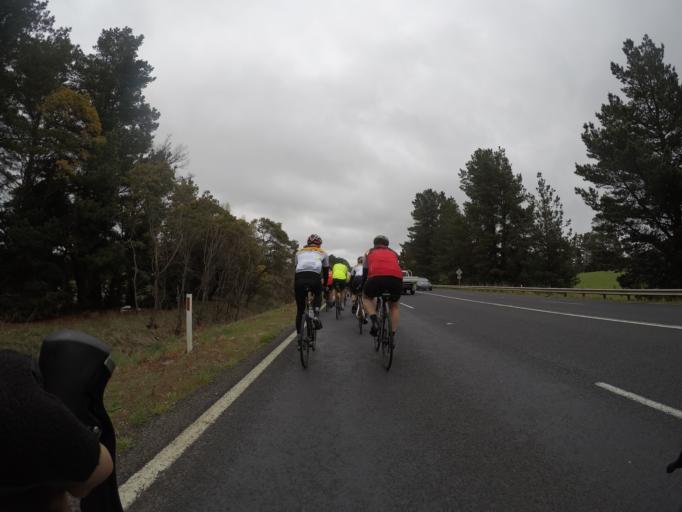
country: AU
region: New South Wales
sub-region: Lithgow
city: Portland
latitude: -33.4332
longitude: 149.8954
